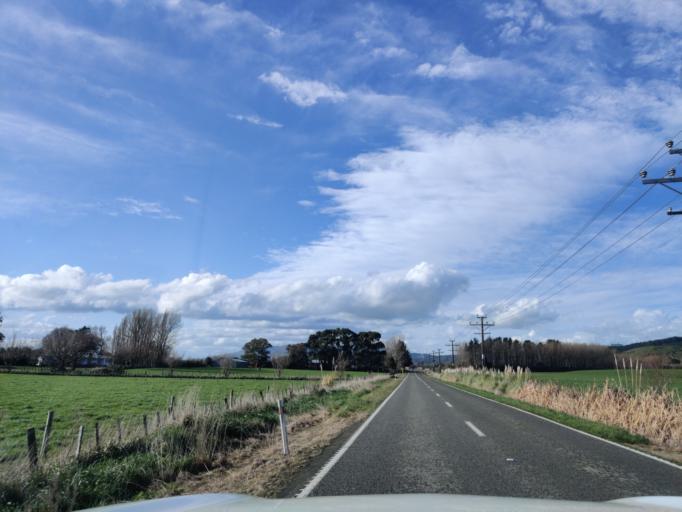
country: NZ
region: Manawatu-Wanganui
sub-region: Palmerston North City
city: Palmerston North
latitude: -40.3409
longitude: 175.7175
